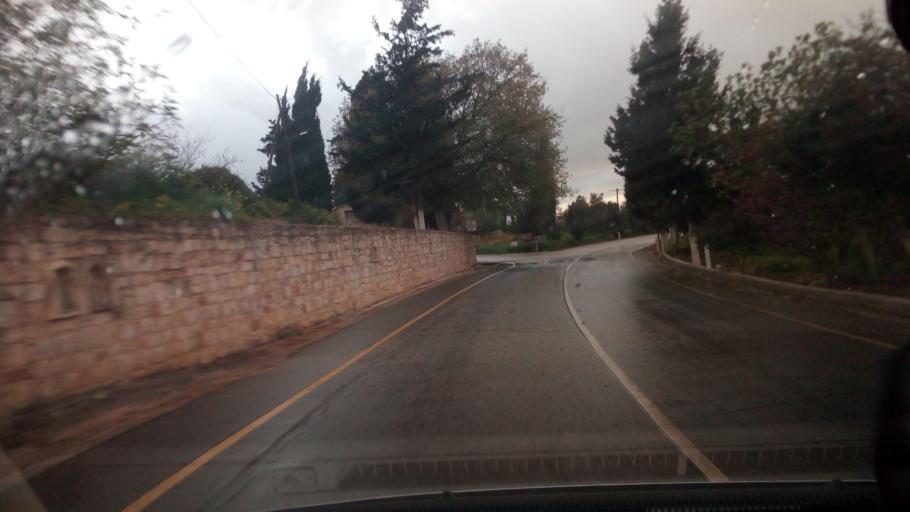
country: CY
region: Pafos
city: Polis
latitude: 34.9627
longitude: 32.4013
